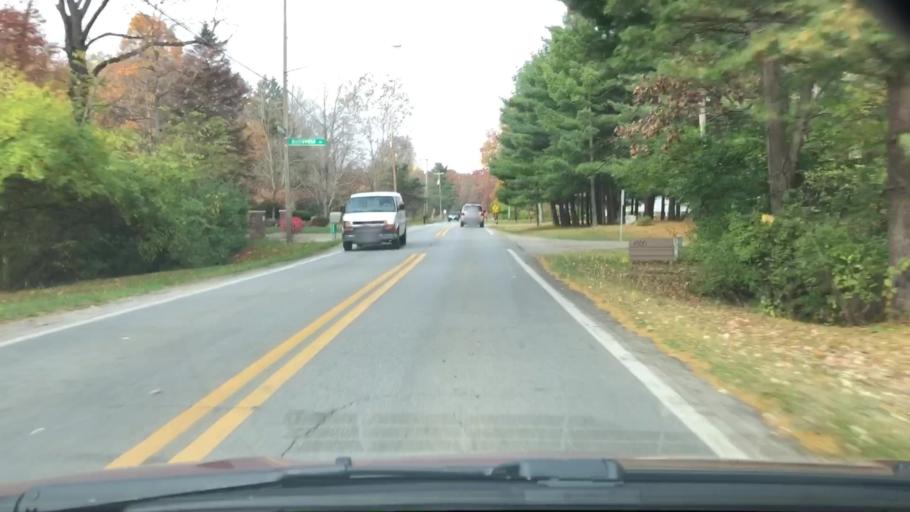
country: US
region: Ohio
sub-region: Franklin County
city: Huber Ridge
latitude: 40.1032
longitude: -82.8693
